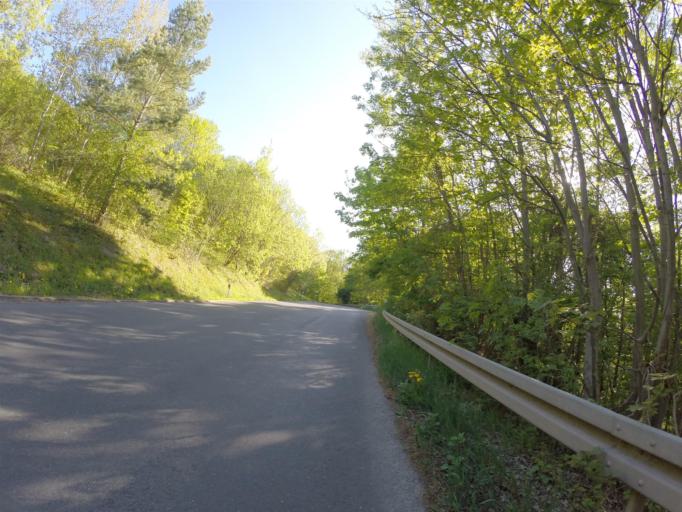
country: DE
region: Thuringia
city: Neuengonna
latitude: 50.9643
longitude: 11.6454
